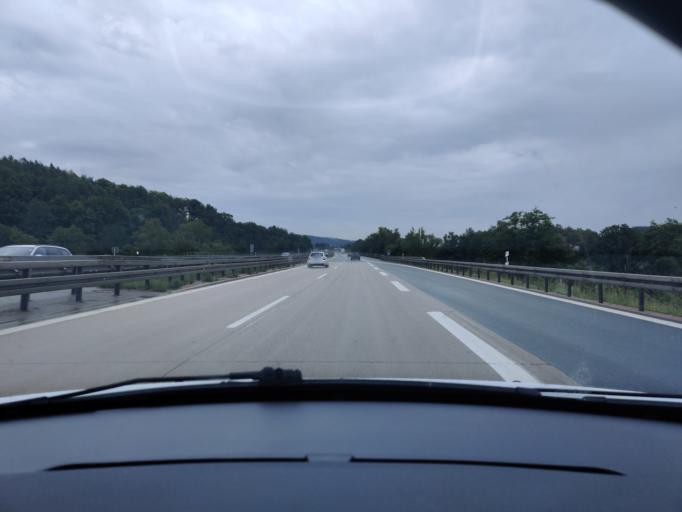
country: DE
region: Bavaria
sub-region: Upper Palatinate
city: Pfreimd
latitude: 49.5140
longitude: 12.1686
